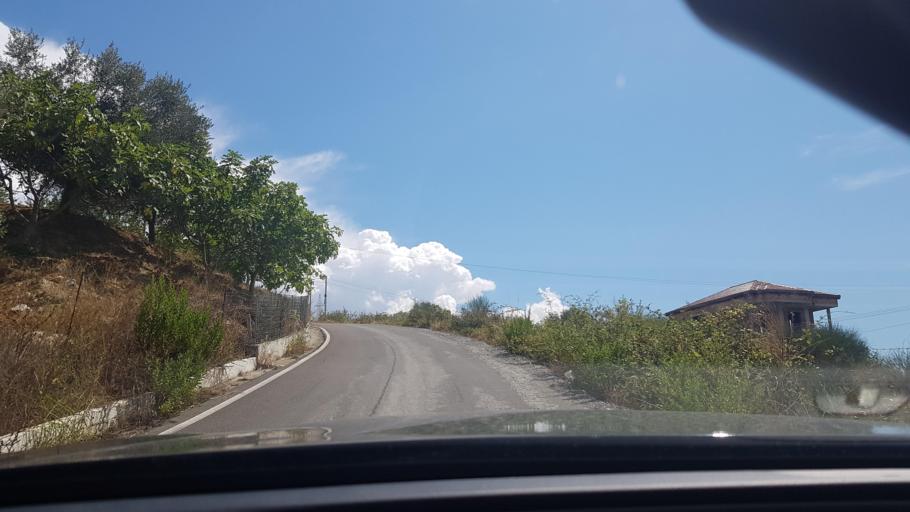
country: AL
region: Durres
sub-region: Rrethi i Durresit
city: Rrashbull
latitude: 41.2966
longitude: 19.5264
